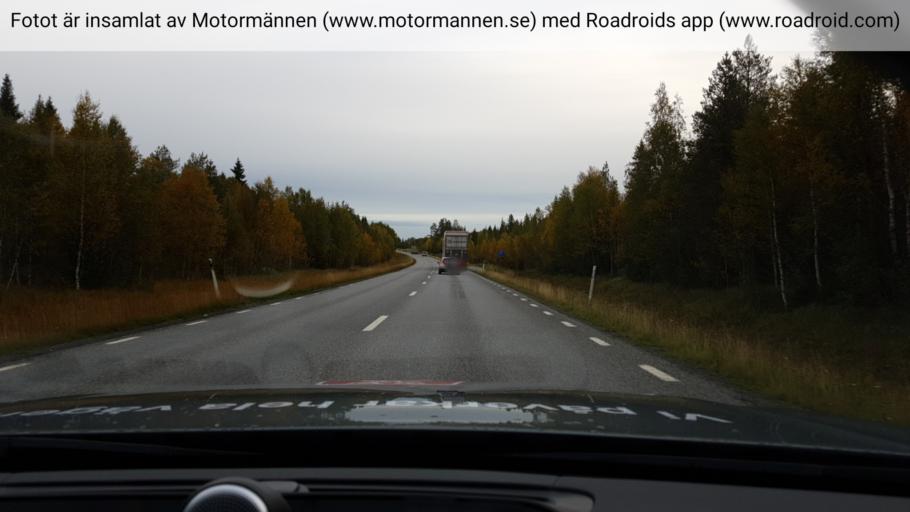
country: SE
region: Jaemtland
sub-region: OEstersunds Kommun
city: Lit
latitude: 63.4268
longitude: 15.1175
